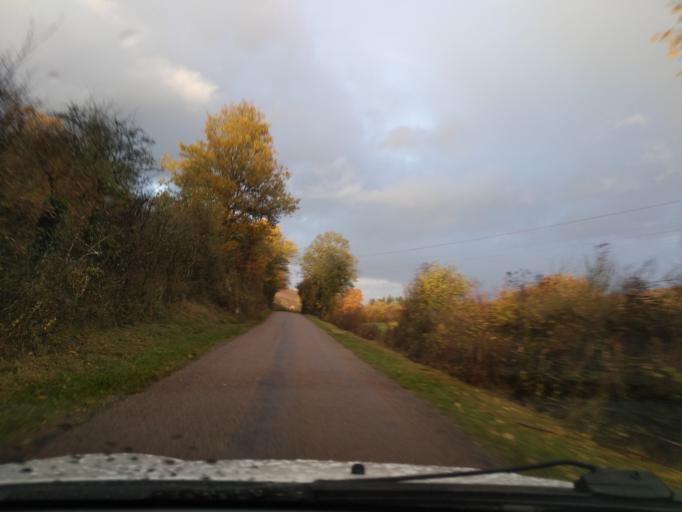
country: FR
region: Bourgogne
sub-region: Departement de Saone-et-Loire
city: Rully
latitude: 46.8853
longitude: 4.7186
